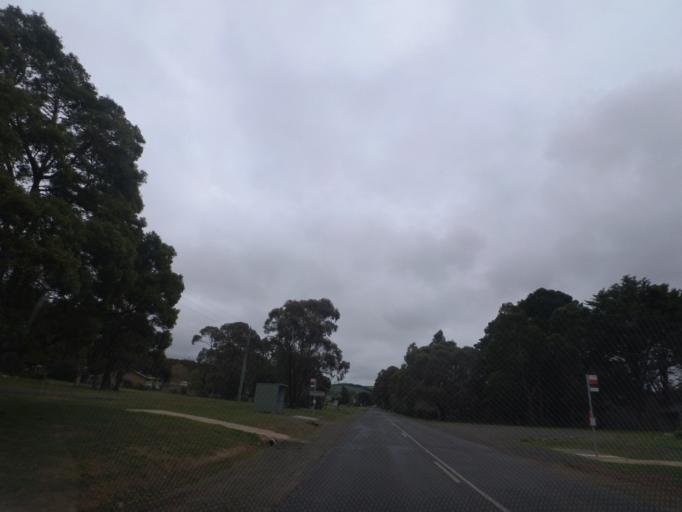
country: AU
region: Victoria
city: Brown Hill
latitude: -37.5853
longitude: 144.1136
